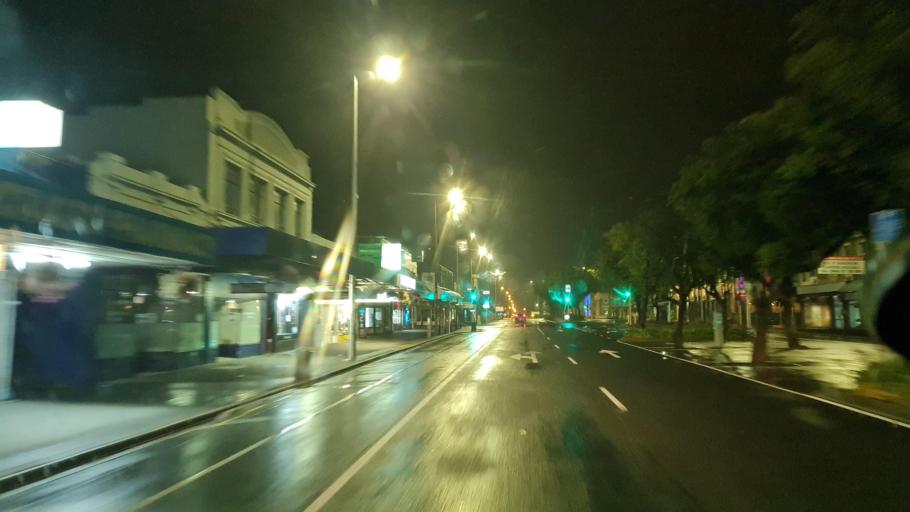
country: NZ
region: Otago
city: Oamaru
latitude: -45.0959
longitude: 170.9720
